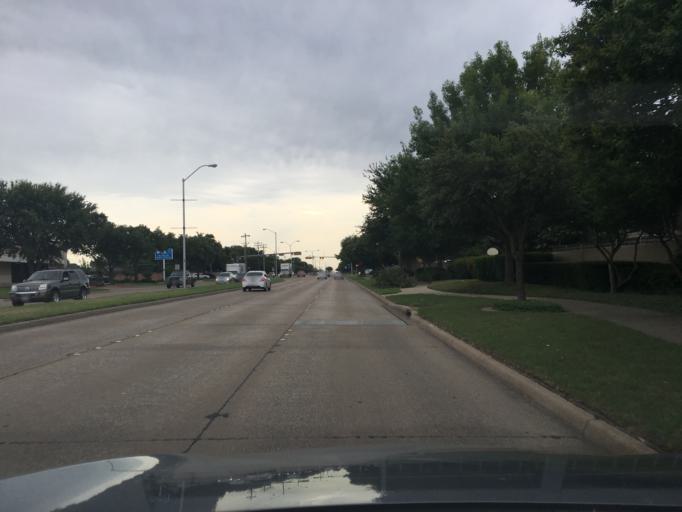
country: US
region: Texas
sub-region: Dallas County
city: Richardson
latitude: 32.9402
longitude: -96.7001
